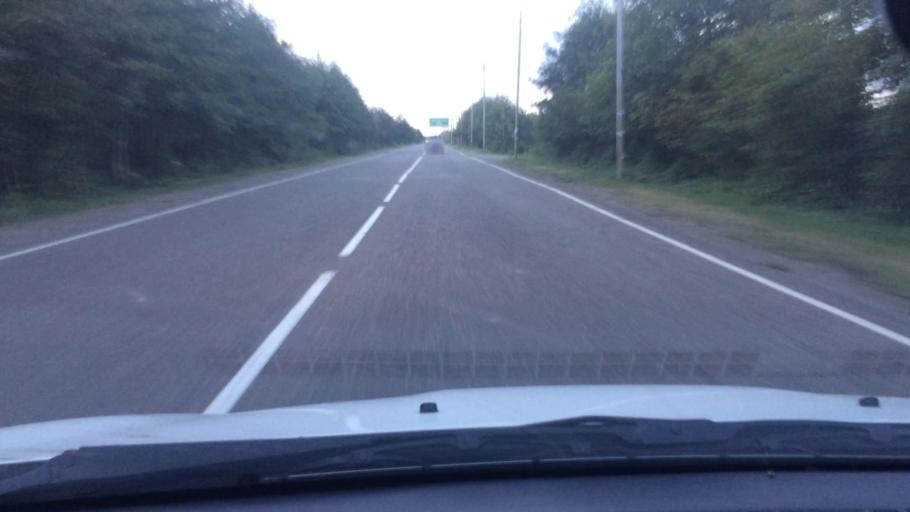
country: GE
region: Guria
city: Urek'i
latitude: 41.9315
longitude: 41.7725
